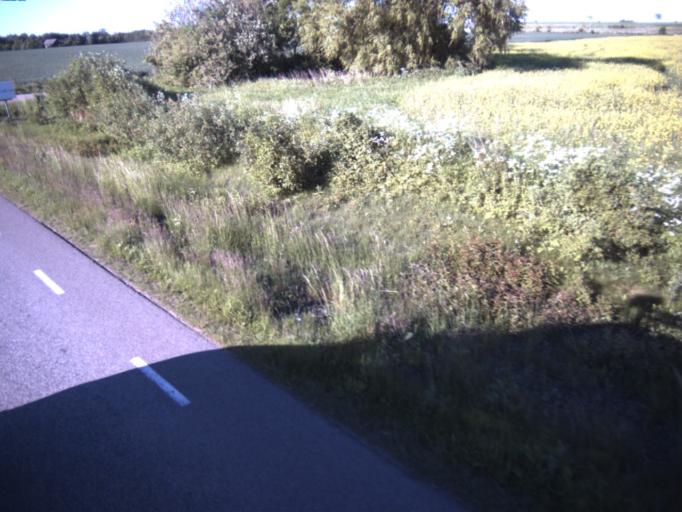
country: SE
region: Skane
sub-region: Helsingborg
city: Rydeback
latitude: 55.9684
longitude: 12.7849
